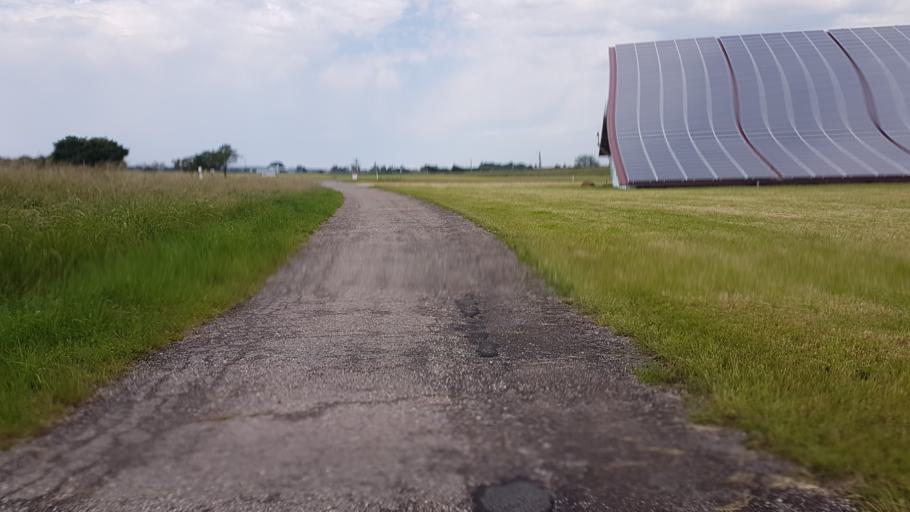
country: DE
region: Baden-Wuerttemberg
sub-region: Freiburg Region
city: Hufingen
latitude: 47.9129
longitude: 8.4886
